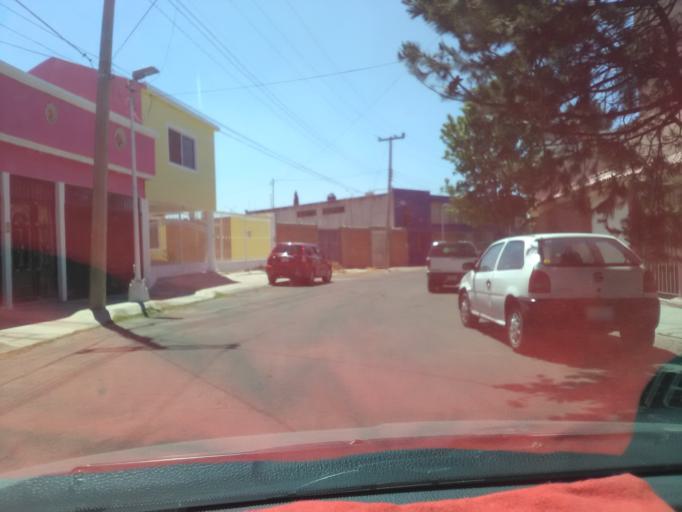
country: MX
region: Durango
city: Victoria de Durango
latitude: 24.0144
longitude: -104.6801
